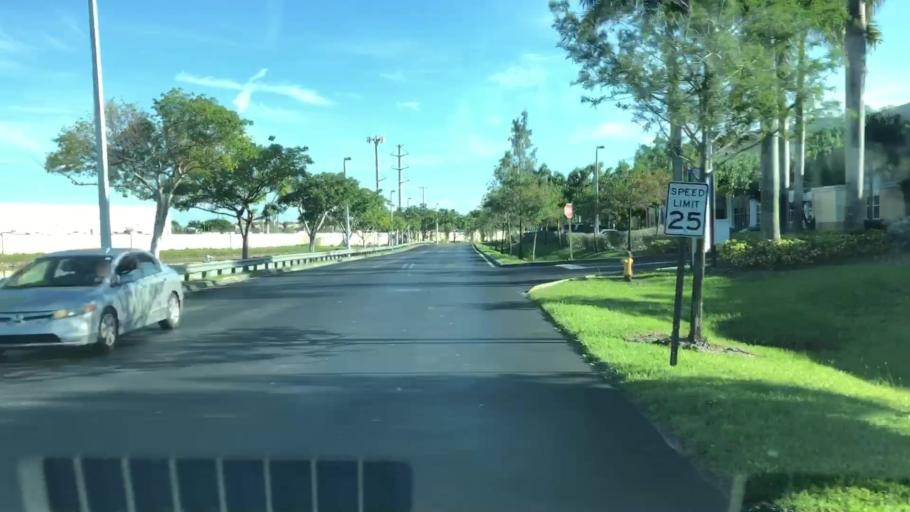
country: US
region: Florida
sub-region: Miami-Dade County
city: Country Club
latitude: 25.9760
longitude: -80.3022
